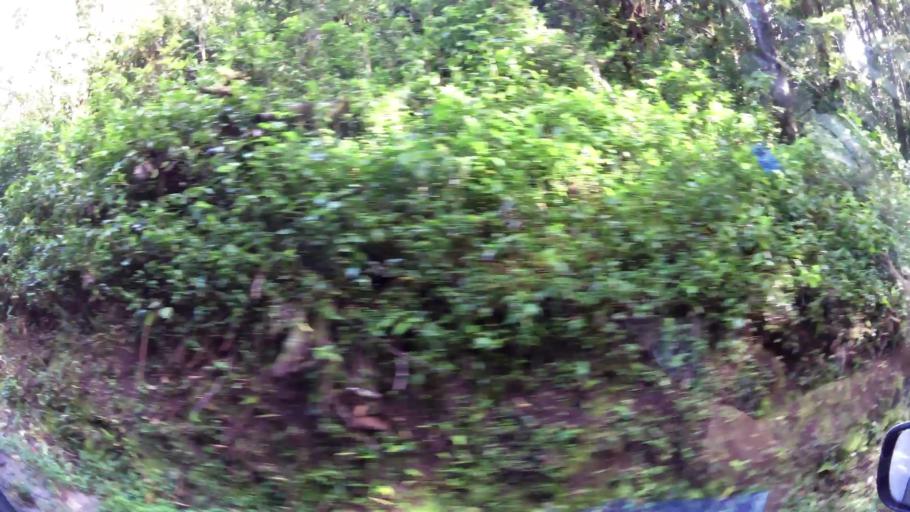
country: CR
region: Guanacaste
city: Juntas
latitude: 10.2995
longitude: -84.7980
